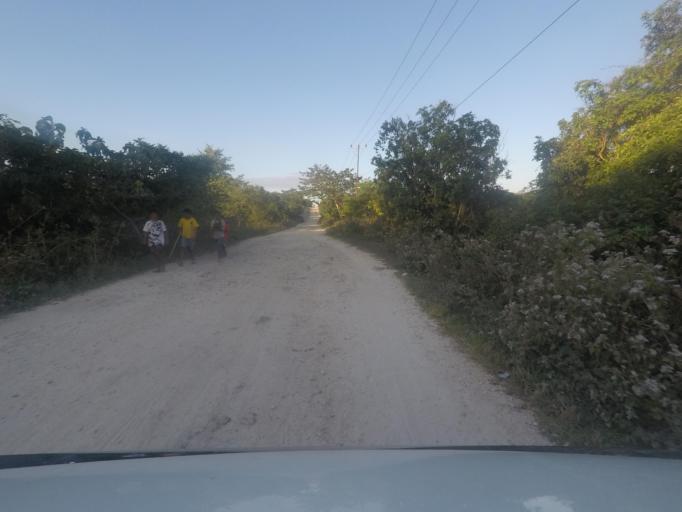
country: TL
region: Lautem
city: Lospalos
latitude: -8.3985
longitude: 127.2066
